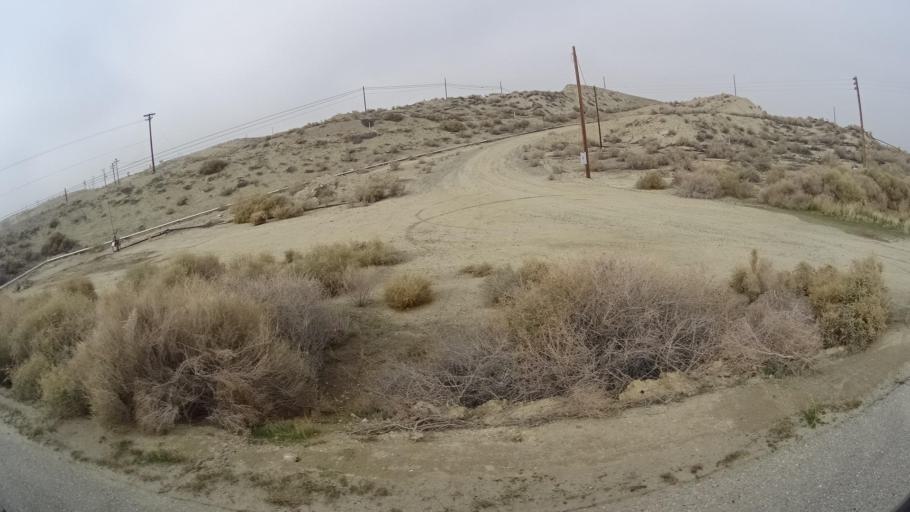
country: US
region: California
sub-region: Kern County
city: Maricopa
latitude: 35.0773
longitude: -119.4007
